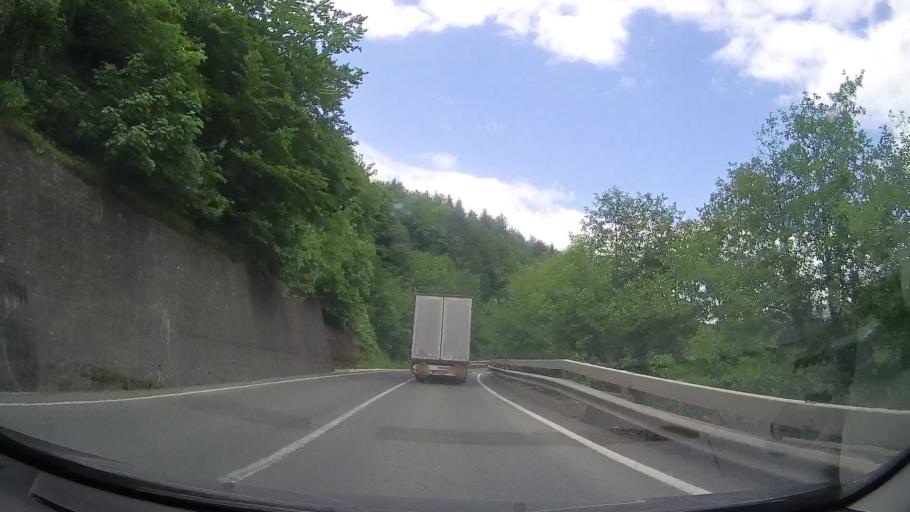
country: RO
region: Prahova
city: Maneciu
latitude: 45.3375
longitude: 25.9620
